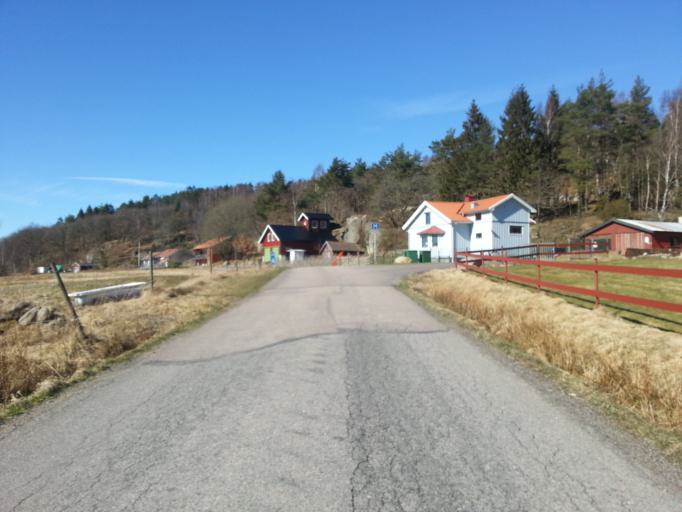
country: SE
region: Vaestra Goetaland
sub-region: Kungalvs Kommun
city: Kungalv
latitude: 57.8998
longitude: 11.9719
